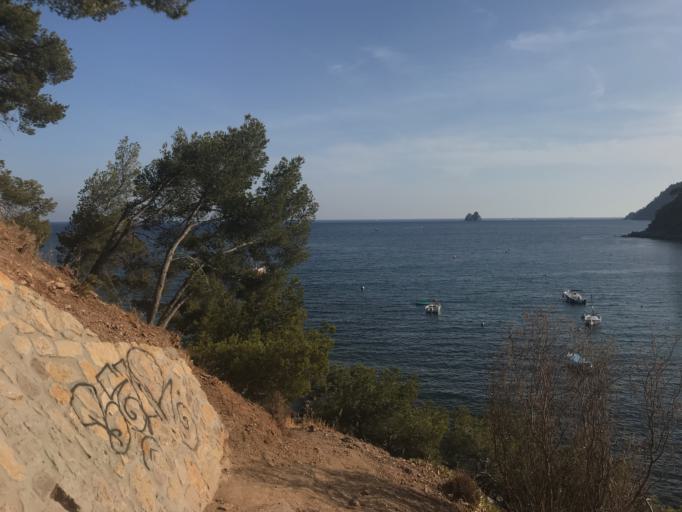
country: FR
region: Provence-Alpes-Cote d'Azur
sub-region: Departement du Var
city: La Seyne-sur-Mer
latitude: 43.0693
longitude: 5.8745
